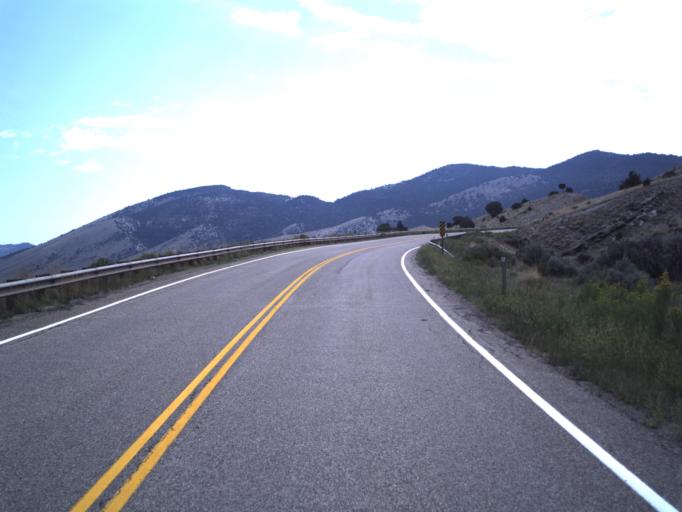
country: US
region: Utah
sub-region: Daggett County
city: Manila
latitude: 40.9200
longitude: -109.6963
